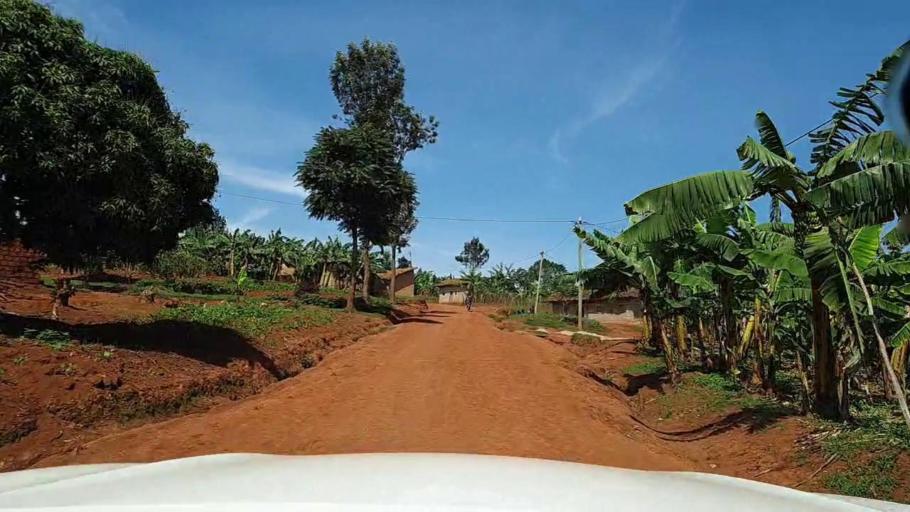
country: RW
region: Southern Province
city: Butare
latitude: -2.7000
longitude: 29.8523
